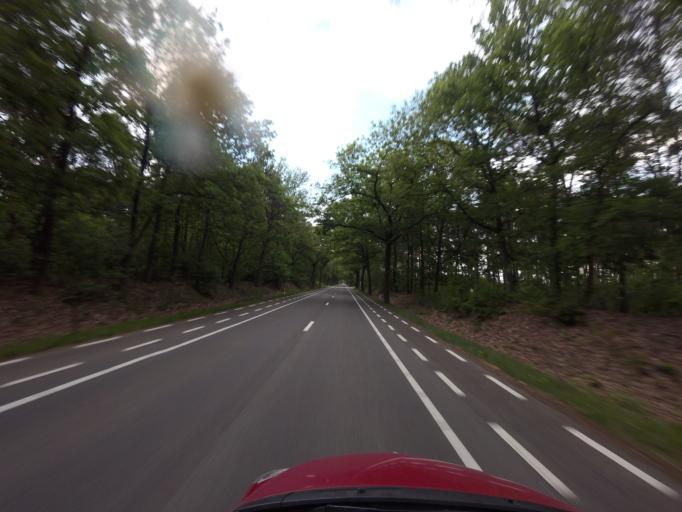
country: BE
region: Flanders
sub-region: Provincie Limburg
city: Overpelt
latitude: 51.1897
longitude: 5.3634
